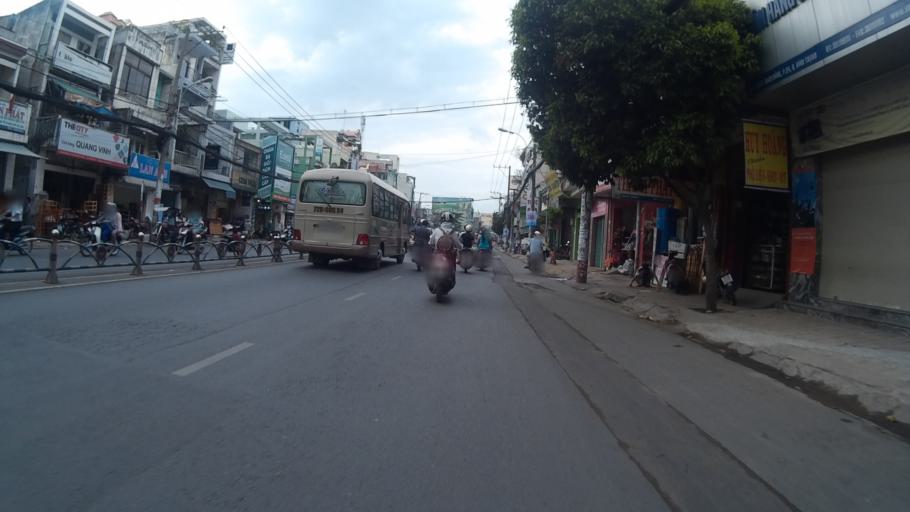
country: VN
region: Ho Chi Minh City
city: Quan Binh Thanh
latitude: 10.8034
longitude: 106.7044
